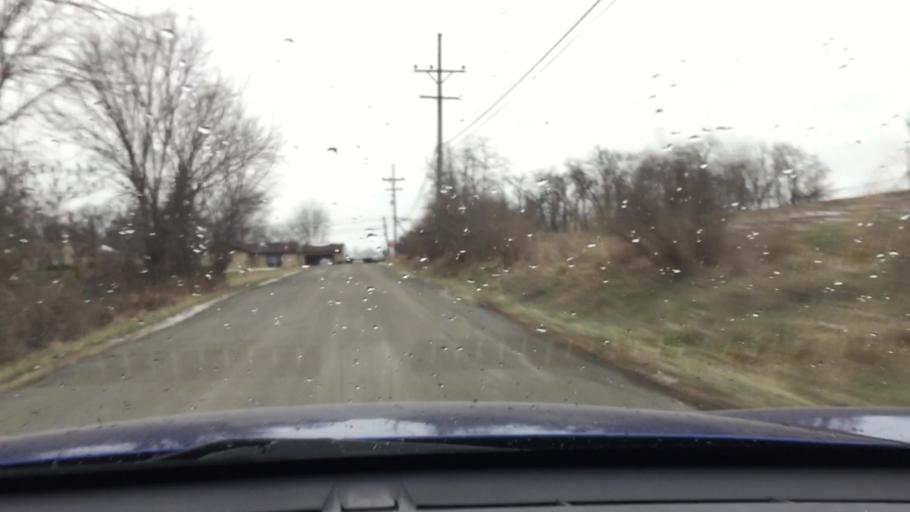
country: US
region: Pennsylvania
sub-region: Westmoreland County
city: Fellsburg
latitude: 40.1638
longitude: -79.8302
